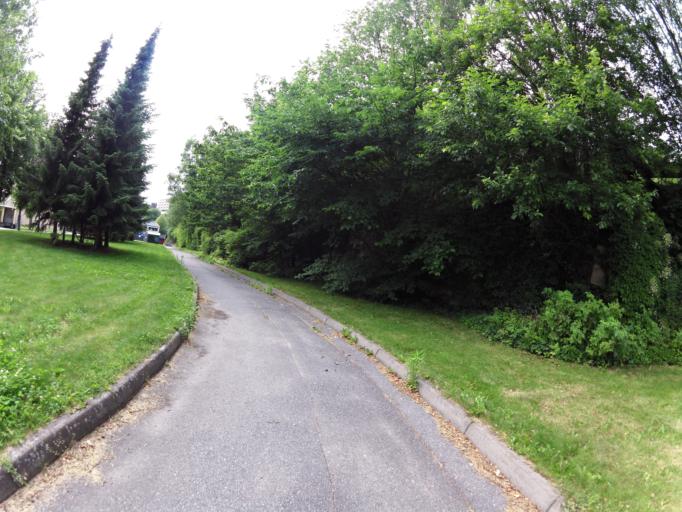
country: NO
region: Ostfold
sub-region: Fredrikstad
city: Fredrikstad
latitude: 59.2189
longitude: 10.9663
